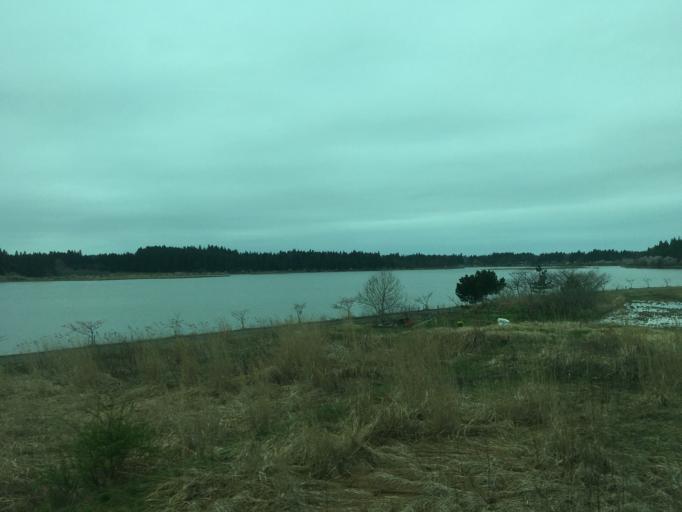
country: JP
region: Akita
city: Noshiromachi
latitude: 40.0929
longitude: 140.0756
